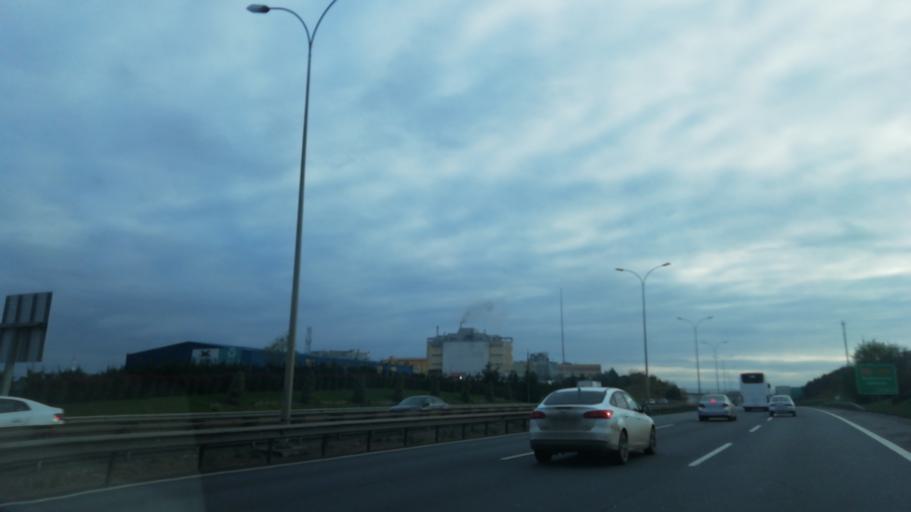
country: TR
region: Istanbul
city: Samandira
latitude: 40.9906
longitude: 29.1811
